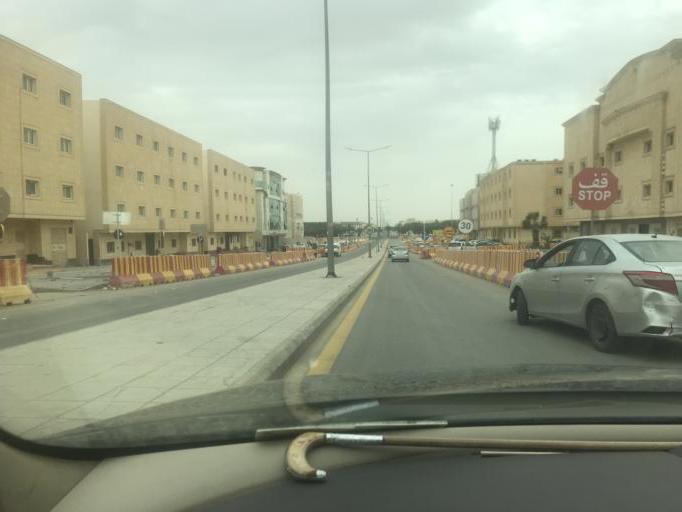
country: SA
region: Ar Riyad
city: Riyadh
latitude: 24.7909
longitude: 46.7111
